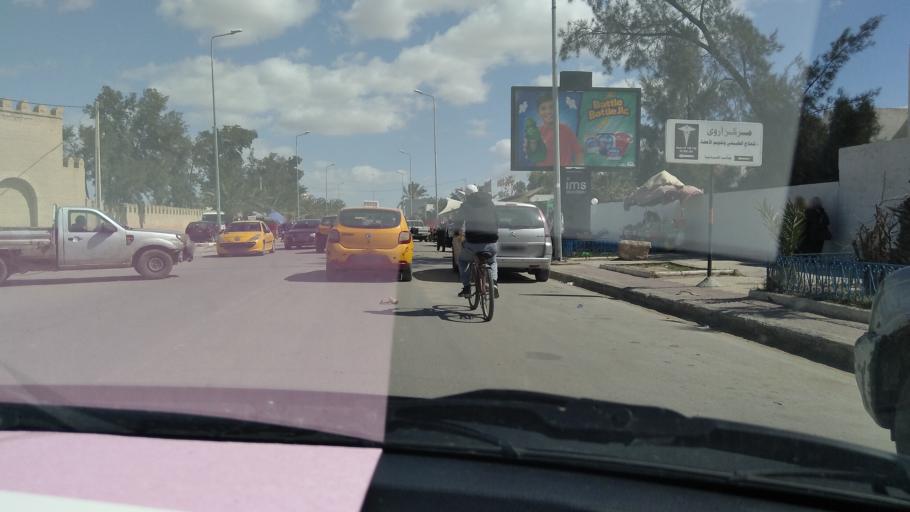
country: TN
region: Al Qayrawan
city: Kairouan
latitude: 35.6850
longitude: 10.0949
